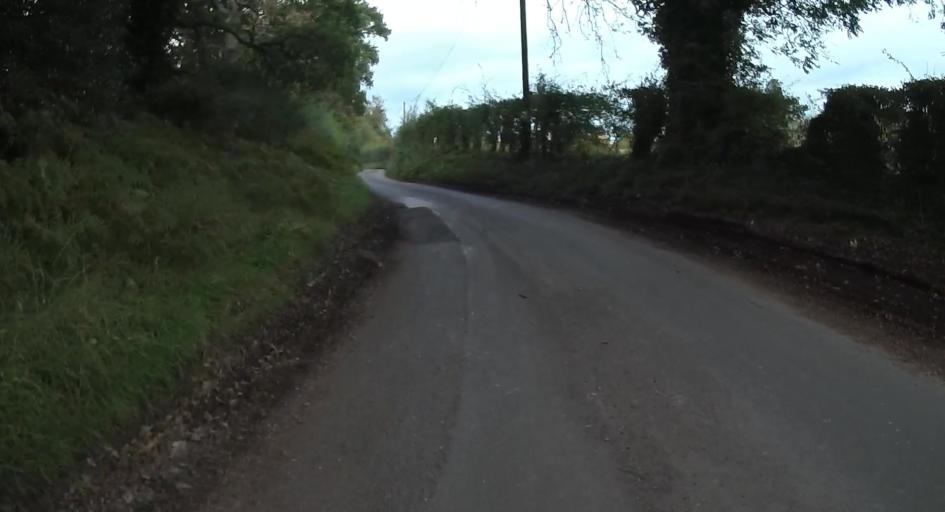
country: GB
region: England
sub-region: Hampshire
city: Kingsley
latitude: 51.1478
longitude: -0.9193
